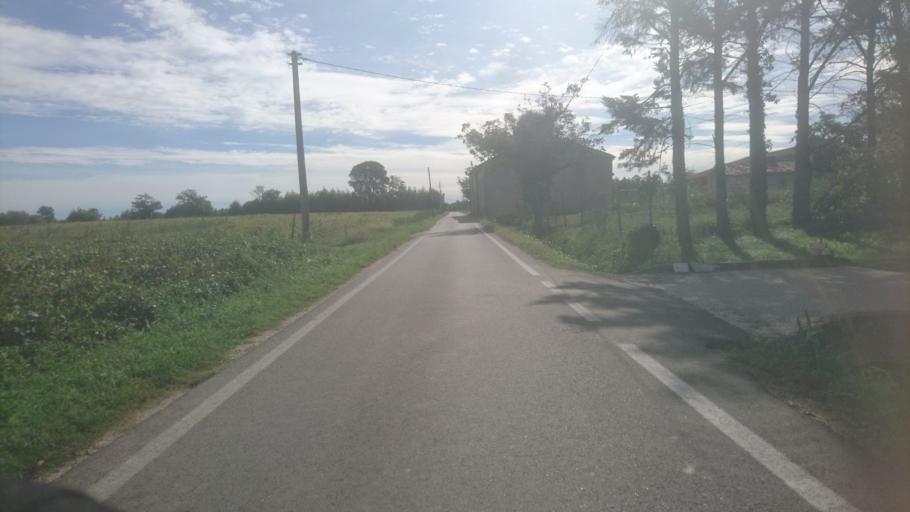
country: IT
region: Veneto
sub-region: Provincia di Vicenza
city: Montegalda
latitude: 45.4658
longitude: 11.6837
